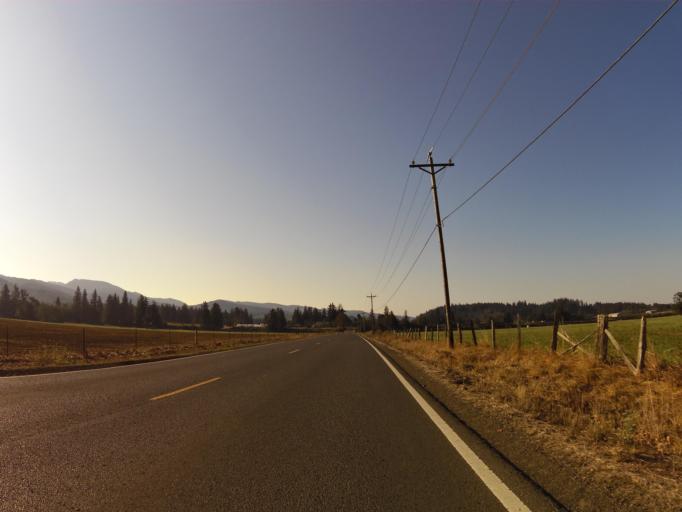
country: US
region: Oregon
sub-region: Tillamook County
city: Tillamook
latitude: 45.4369
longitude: -123.7777
